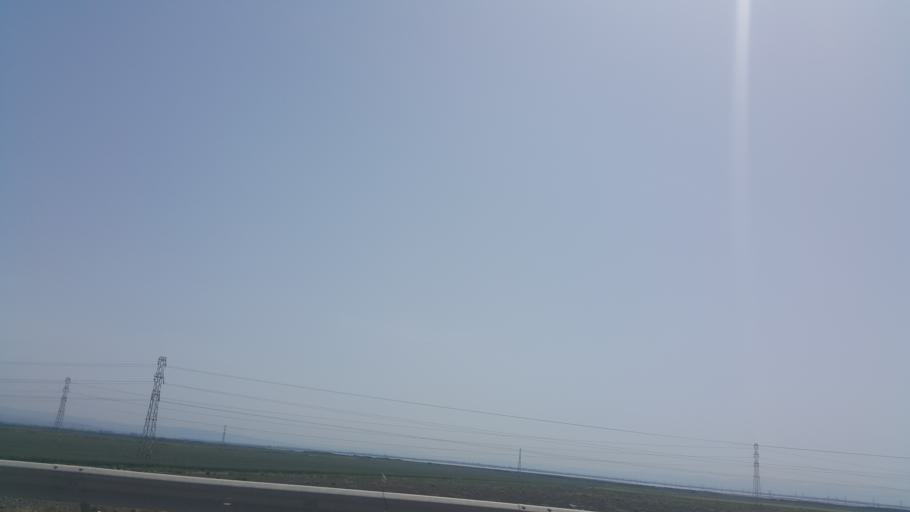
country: TR
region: Hatay
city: Serinyol
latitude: 36.4221
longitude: 36.2750
